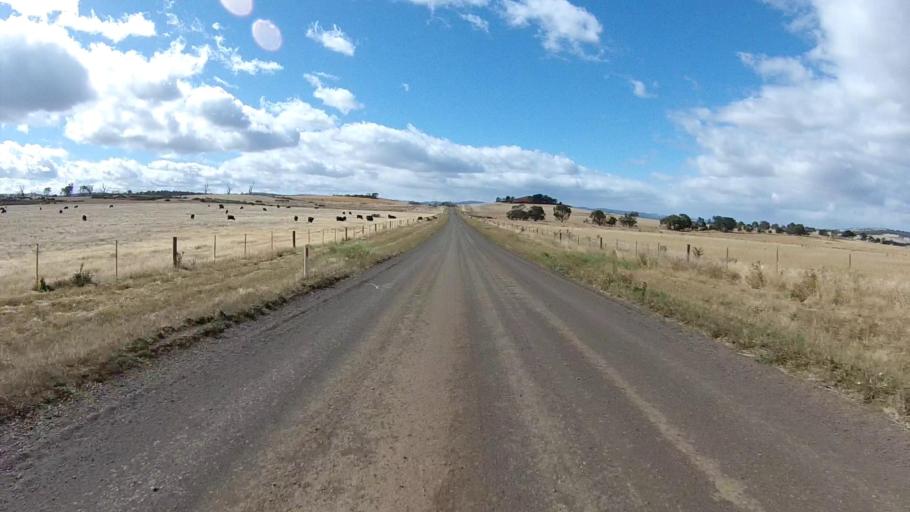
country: AU
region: Tasmania
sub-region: Northern Midlands
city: Evandale
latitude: -41.7126
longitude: 147.4127
